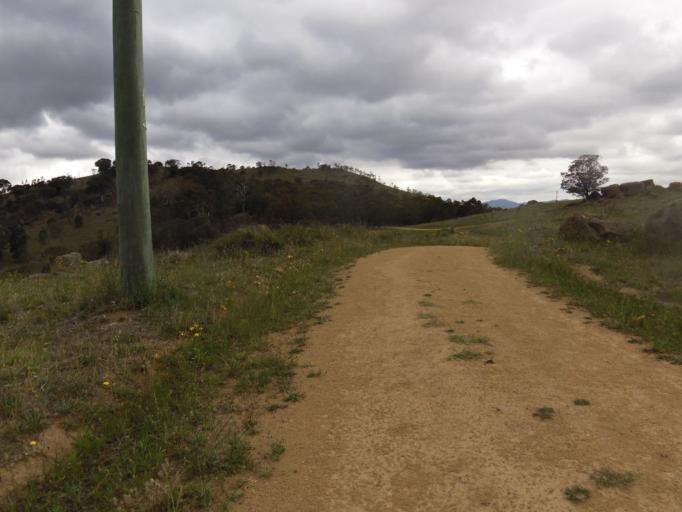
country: AU
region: Australian Capital Territory
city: Macarthur
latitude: -35.3653
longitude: 149.0410
